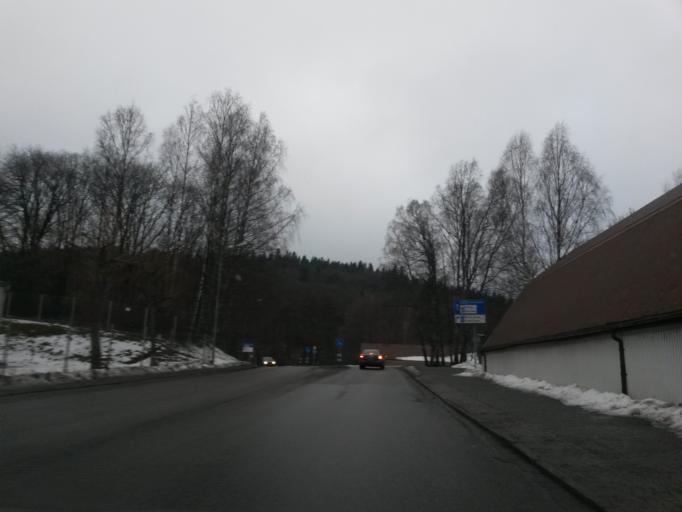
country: SE
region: Vaestra Goetaland
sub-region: Boras Kommun
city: Boras
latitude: 57.7348
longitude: 12.9314
